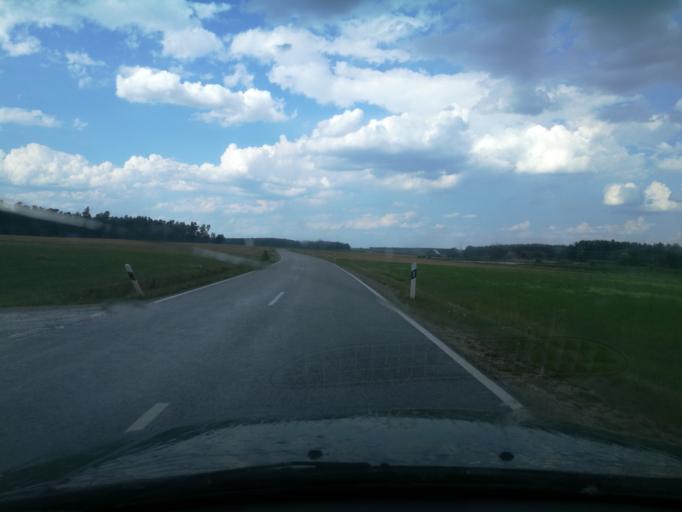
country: DE
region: Bavaria
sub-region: Regierungsbezirk Mittelfranken
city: Wilhermsdorf
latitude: 49.4530
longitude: 10.7511
